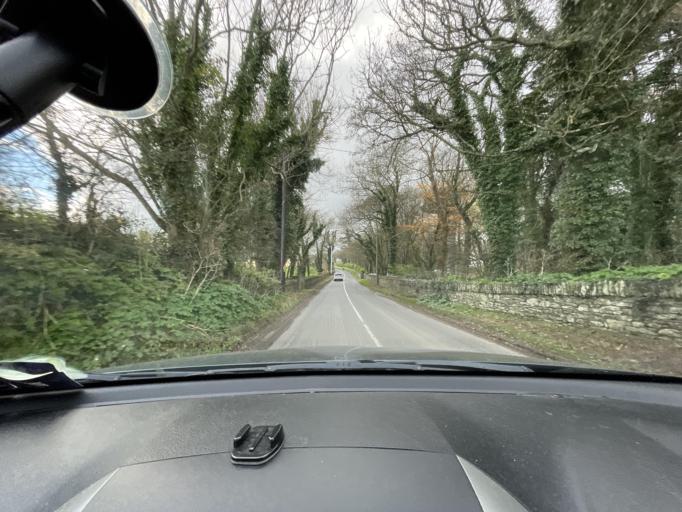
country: IE
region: Leinster
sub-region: Lu
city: Clogherhead
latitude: 53.7868
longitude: -6.2423
